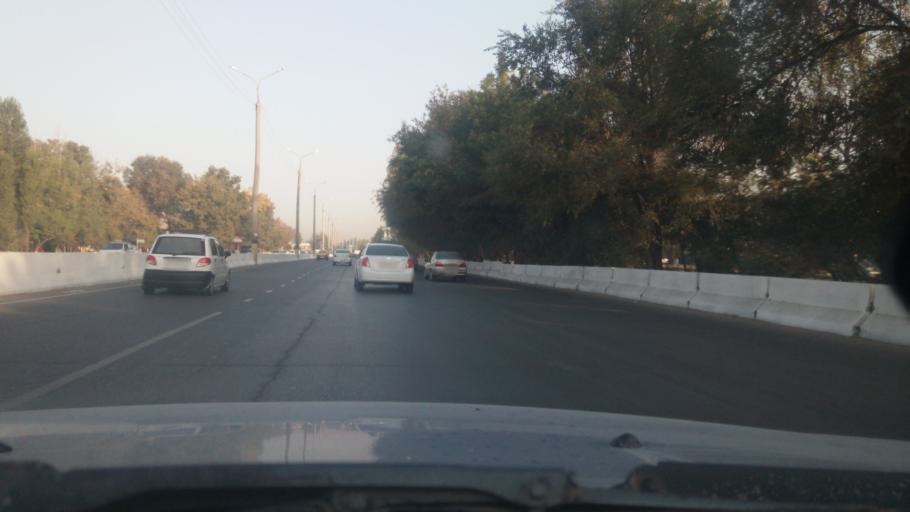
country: UZ
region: Toshkent Shahri
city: Tashkent
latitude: 41.2570
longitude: 69.1541
